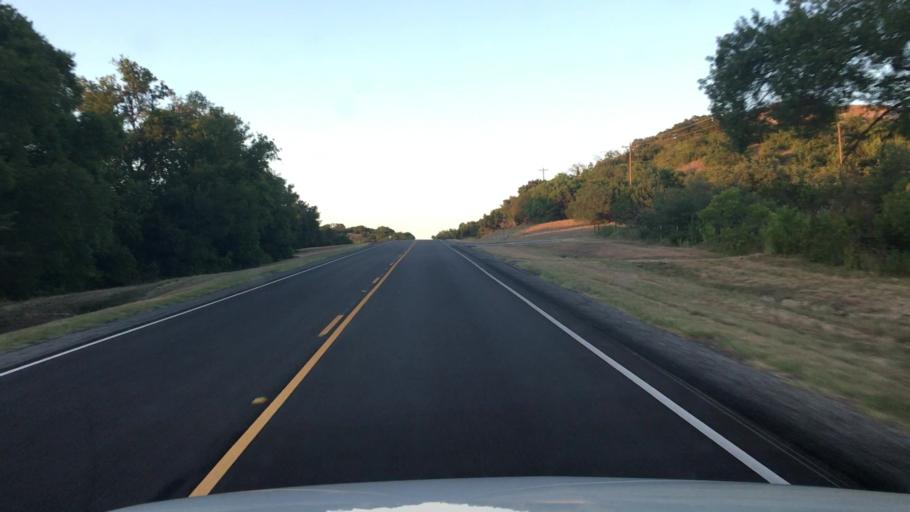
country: US
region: Texas
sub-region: Hamilton County
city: Hico
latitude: 32.0951
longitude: -97.9680
